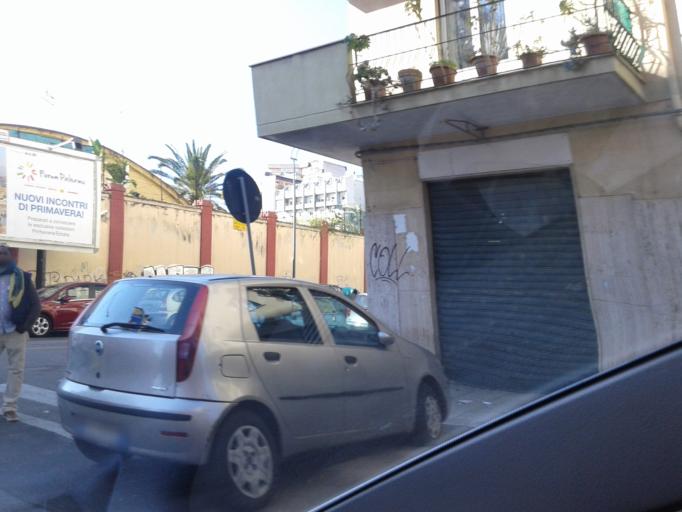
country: IT
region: Sicily
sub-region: Palermo
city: Palermo
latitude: 38.1302
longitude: 13.3435
